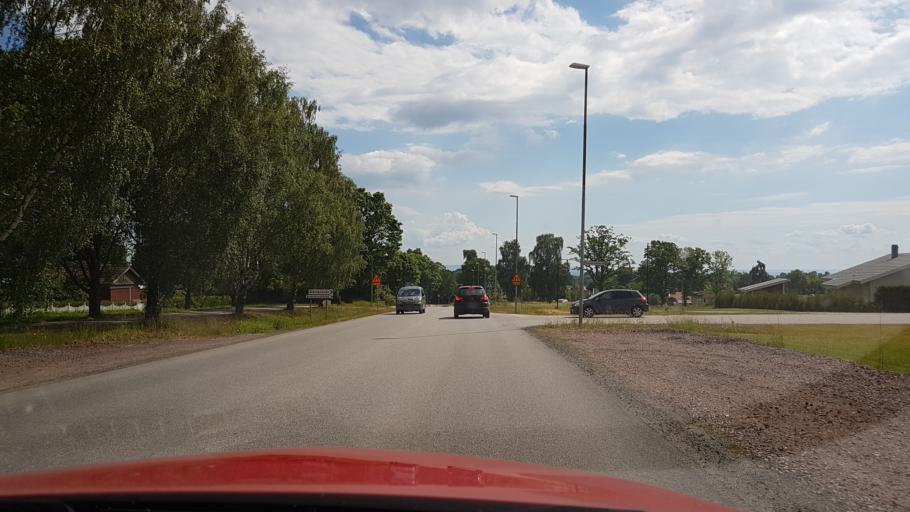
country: SE
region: Vaestra Goetaland
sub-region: Hjo Kommun
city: Hjo
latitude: 58.3028
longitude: 14.2663
